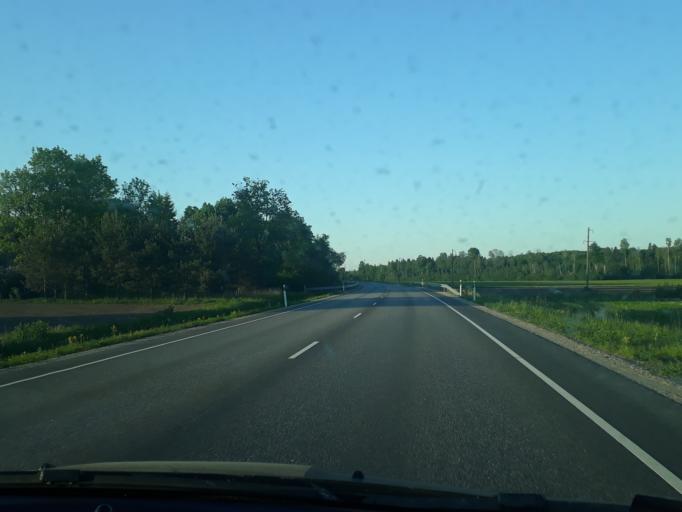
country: EE
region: Paernumaa
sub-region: Tootsi vald
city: Tootsi
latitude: 58.5593
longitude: 24.8651
